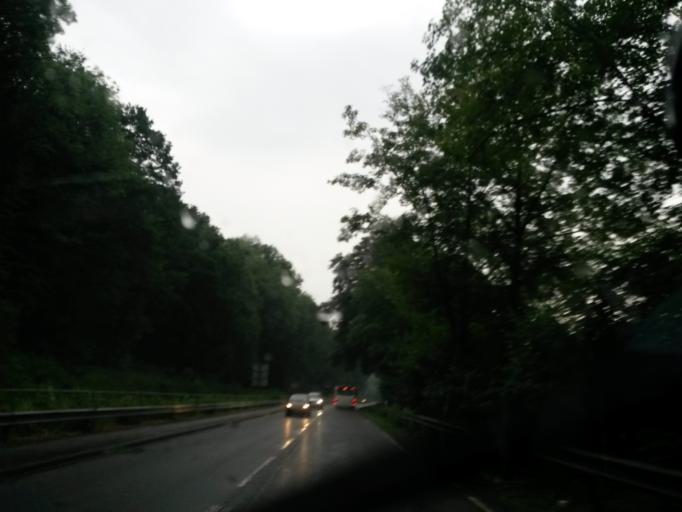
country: DE
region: North Rhine-Westphalia
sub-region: Regierungsbezirk Koln
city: Engelskirchen
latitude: 50.9879
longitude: 7.4340
